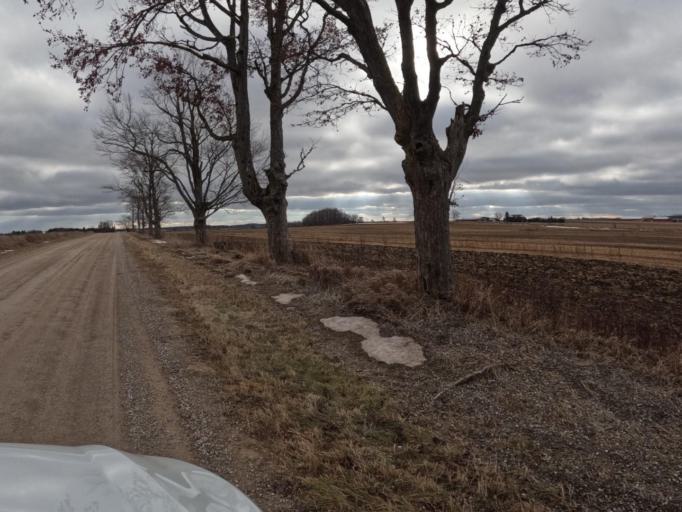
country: CA
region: Ontario
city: Shelburne
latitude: 43.8791
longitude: -80.4039
